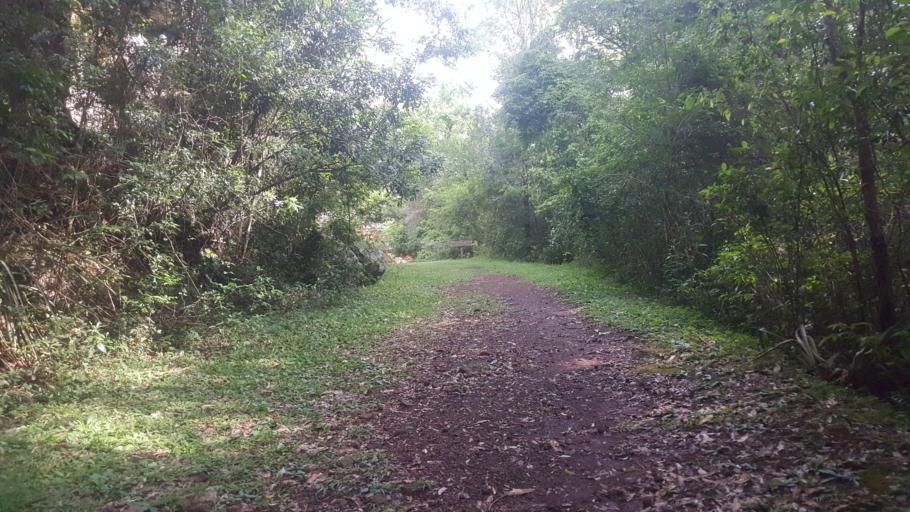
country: AR
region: Misiones
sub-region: Departamento de Candelaria
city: Candelaria
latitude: -27.5598
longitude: -55.7099
